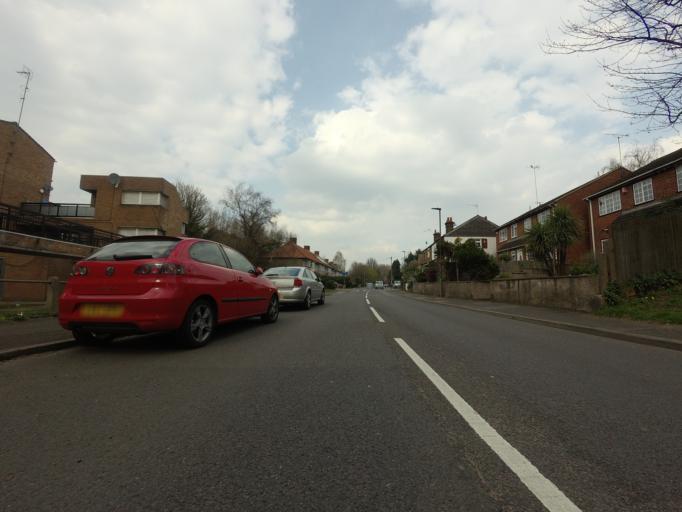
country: GB
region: England
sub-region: Greater London
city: Sidcup
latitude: 51.4004
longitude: 0.1161
